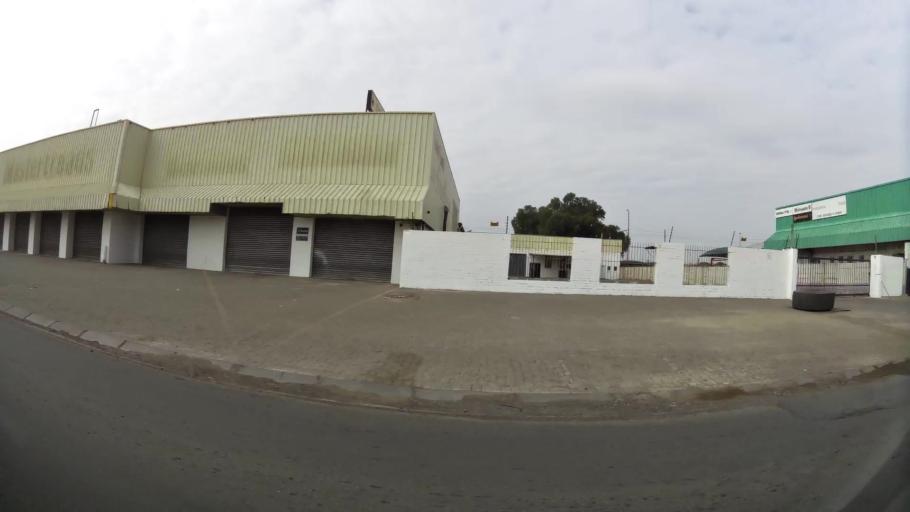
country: ZA
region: Orange Free State
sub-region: Mangaung Metropolitan Municipality
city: Bloemfontein
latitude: -29.1322
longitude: 26.2213
